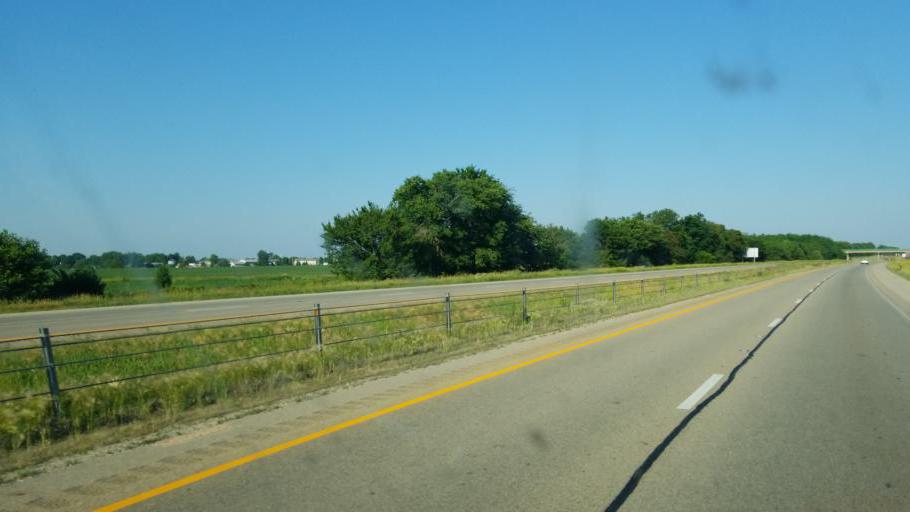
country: US
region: Illinois
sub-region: LaSalle County
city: Ottawa
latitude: 41.3768
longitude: -88.8103
